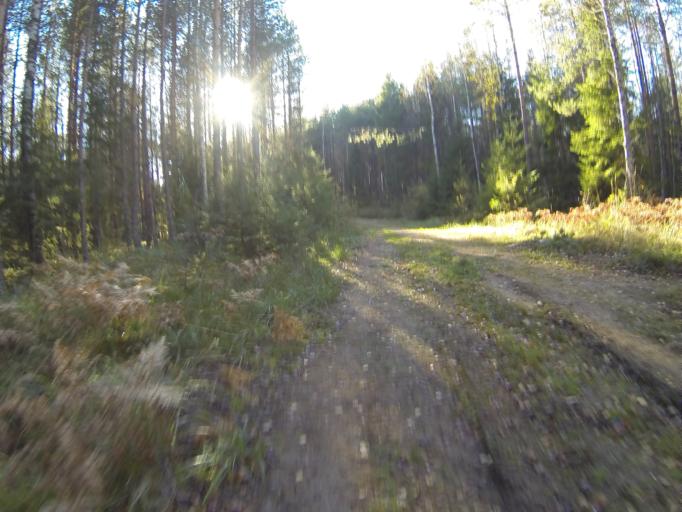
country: FI
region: Varsinais-Suomi
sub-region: Salo
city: Saerkisalo
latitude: 60.2238
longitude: 22.9445
